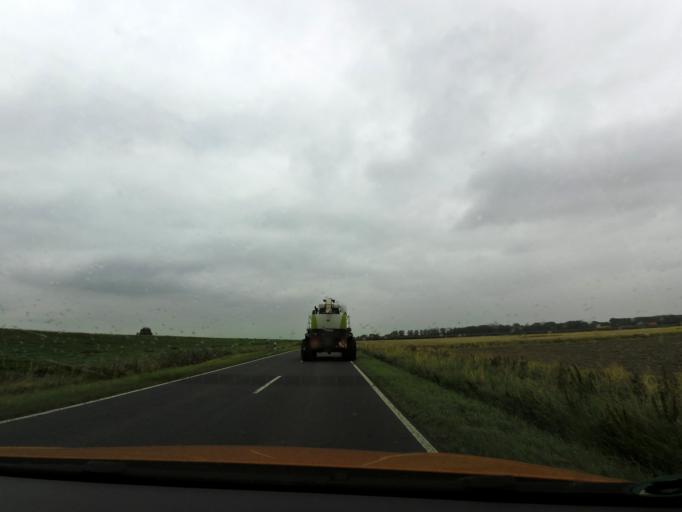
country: DE
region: Lower Saxony
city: Wirdum
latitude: 53.5127
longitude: 7.1233
